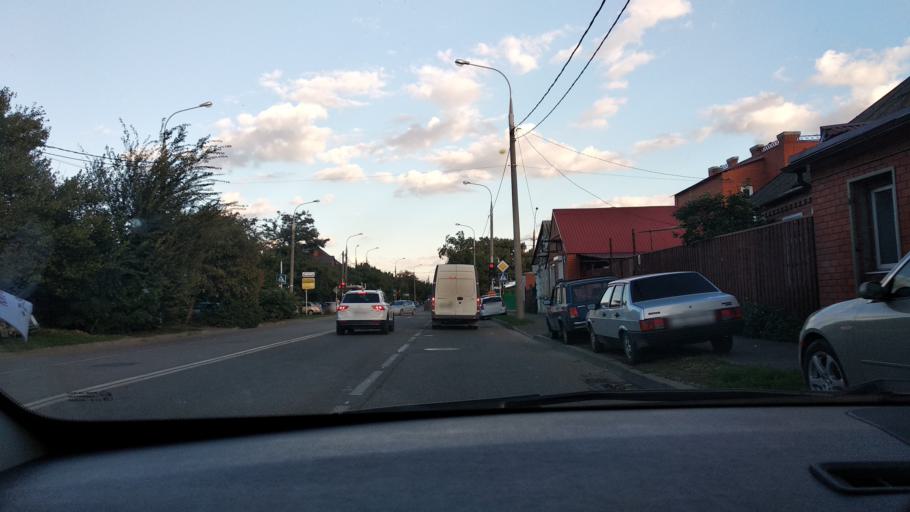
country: RU
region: Krasnodarskiy
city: Krasnodar
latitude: 45.0159
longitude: 38.9960
